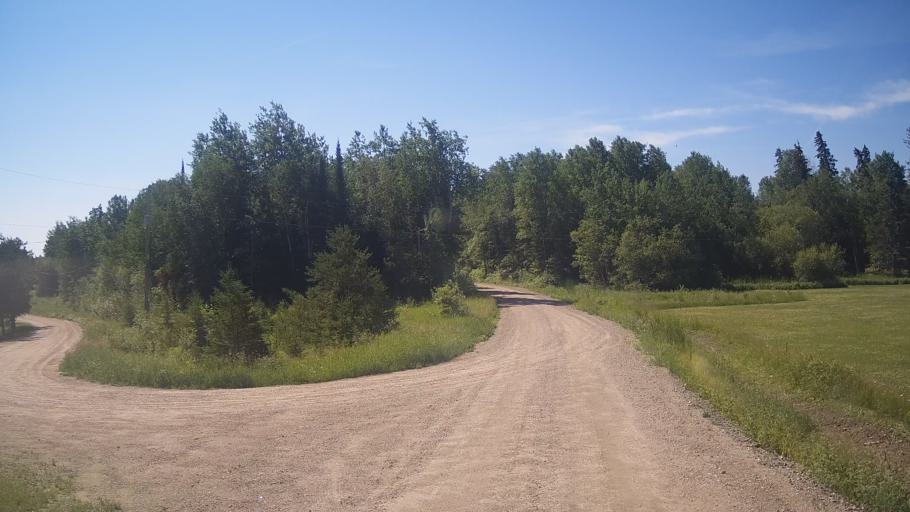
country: CA
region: Ontario
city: Dryden
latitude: 49.8221
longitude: -93.3388
